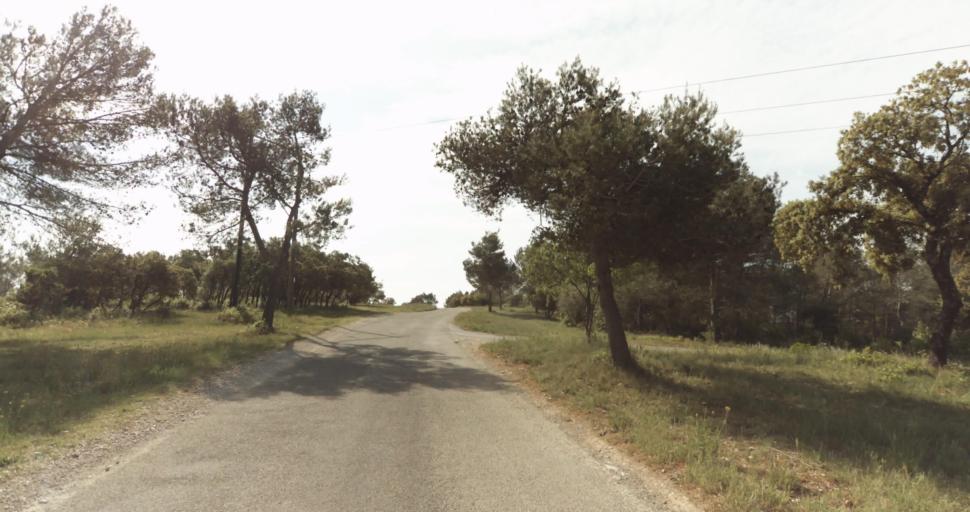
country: FR
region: Languedoc-Roussillon
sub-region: Departement du Gard
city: Poulx
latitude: 43.8801
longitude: 4.3889
